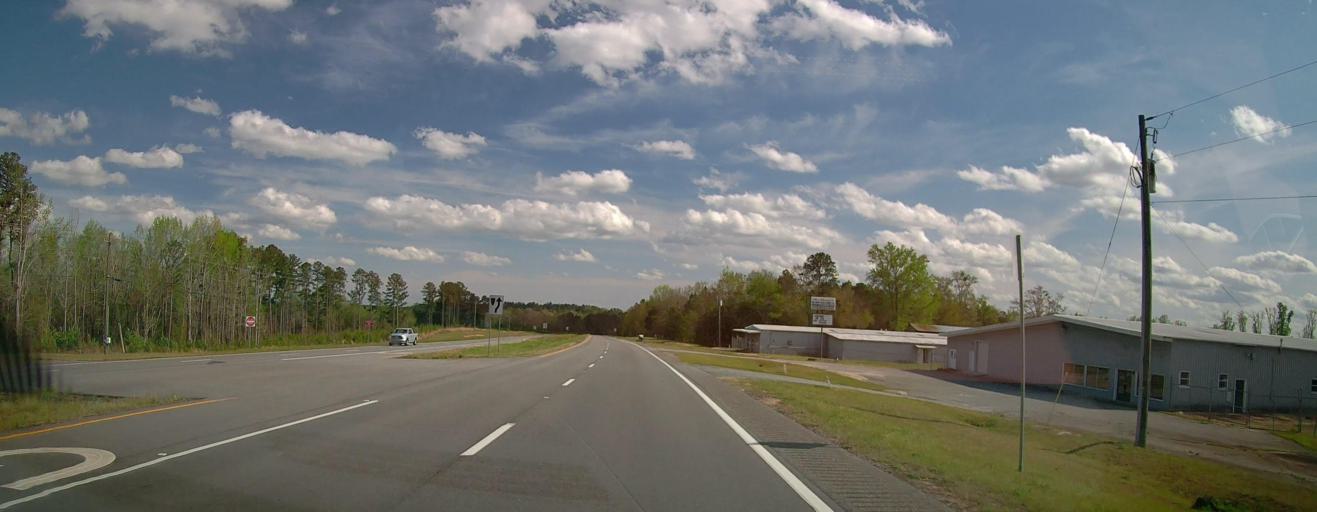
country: US
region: Georgia
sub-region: Baldwin County
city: Hardwick
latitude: 33.0130
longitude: -83.2256
